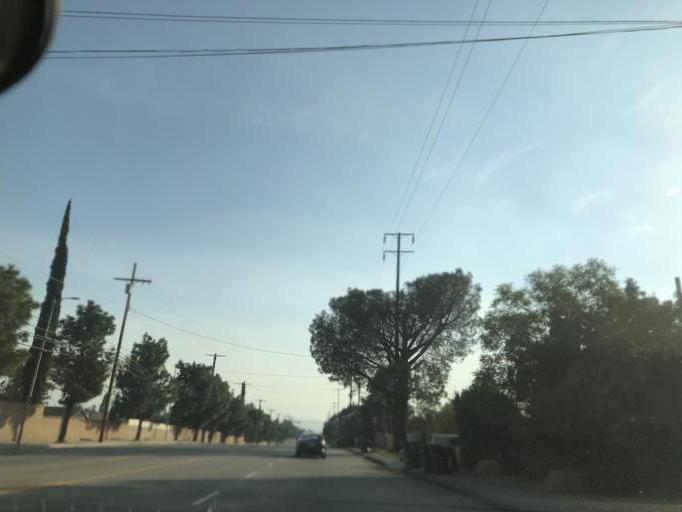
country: US
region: California
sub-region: Los Angeles County
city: Chatsworth
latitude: 34.2678
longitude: -118.5887
